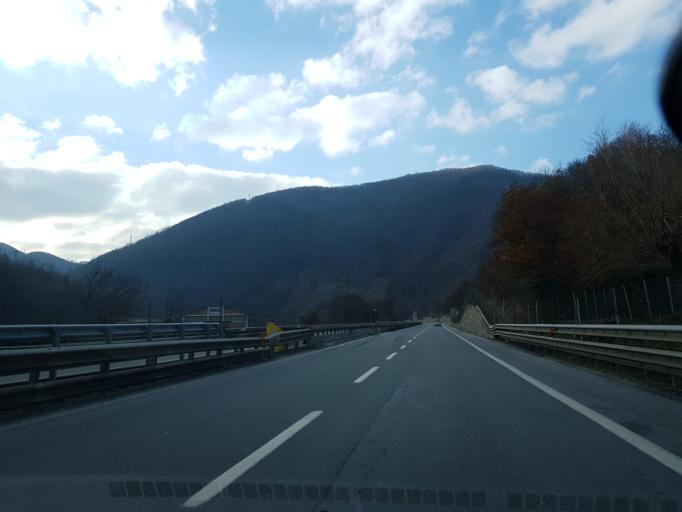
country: IT
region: Liguria
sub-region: Provincia di Genova
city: Isola del Cantone
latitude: 44.6657
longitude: 8.9364
